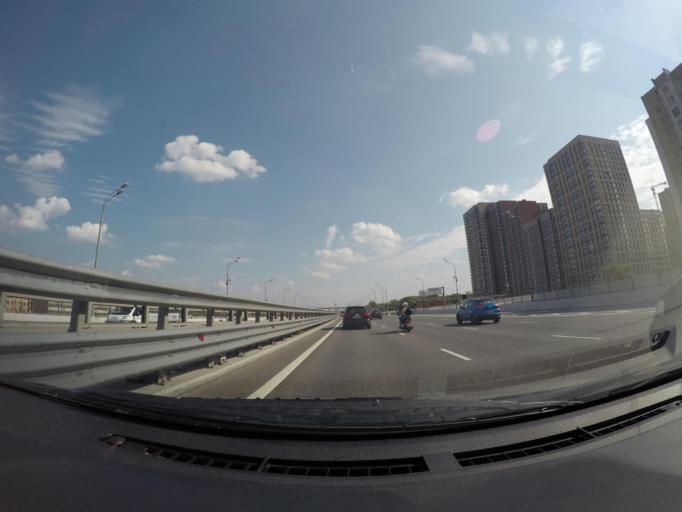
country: RU
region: Moscow
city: Novokhovrino
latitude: 55.8712
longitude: 37.5027
